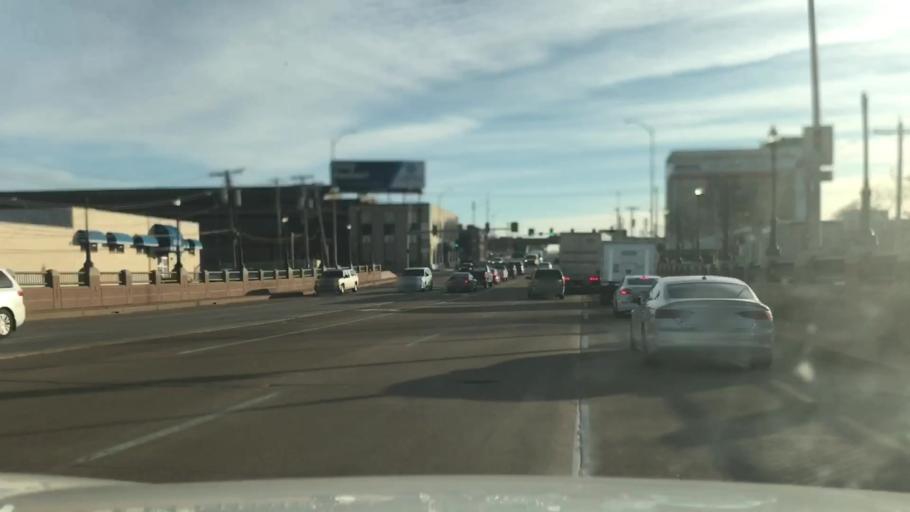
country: US
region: Missouri
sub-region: Saint Louis County
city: Richmond Heights
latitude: 38.6217
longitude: -90.2660
